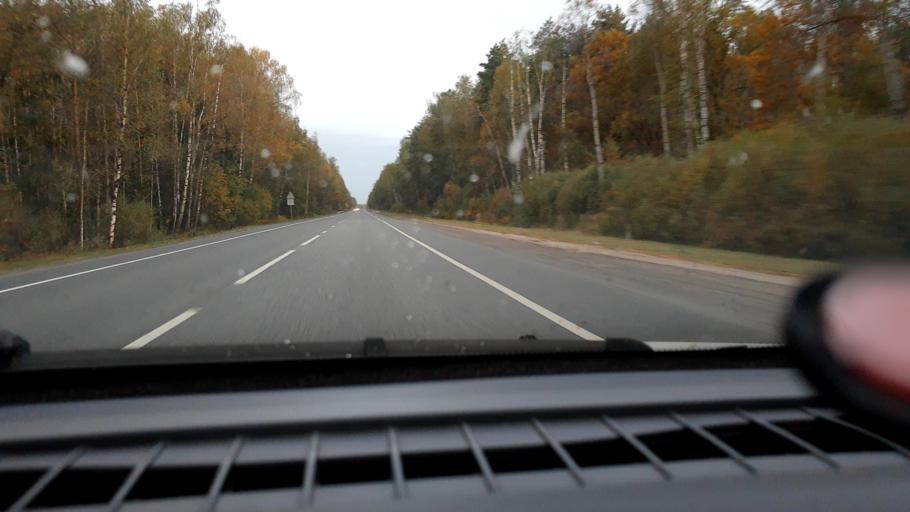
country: RU
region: Vladimir
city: Orgtrud
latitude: 56.2057
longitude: 40.7155
